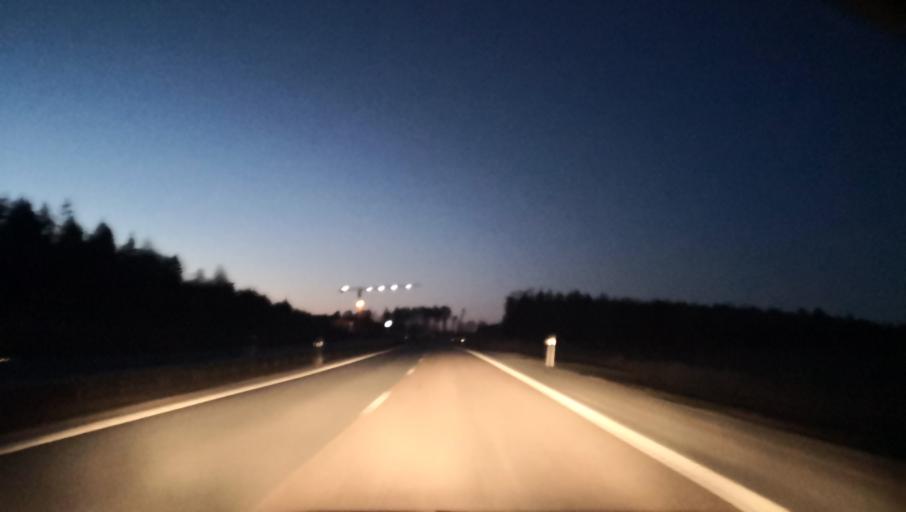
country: SE
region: Stockholm
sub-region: Haninge Kommun
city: Jordbro
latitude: 59.0806
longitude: 18.0788
